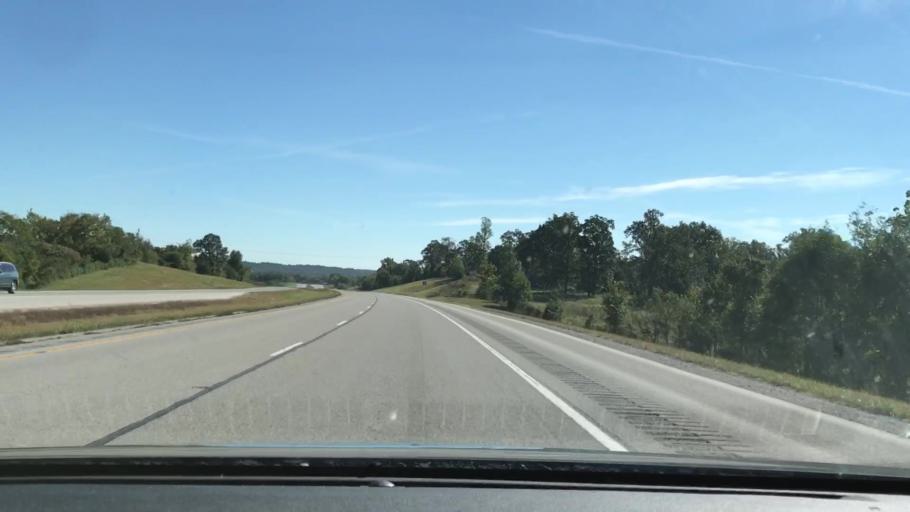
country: US
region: Kentucky
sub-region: Todd County
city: Elkton
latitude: 36.8210
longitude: -87.1899
